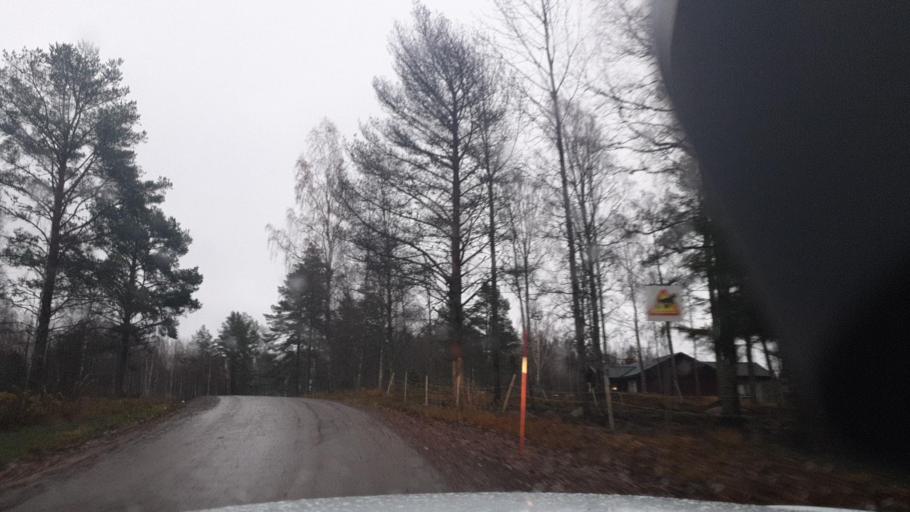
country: NO
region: Hedmark
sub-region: Eidskog
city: Skotterud
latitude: 59.7357
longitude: 12.0873
